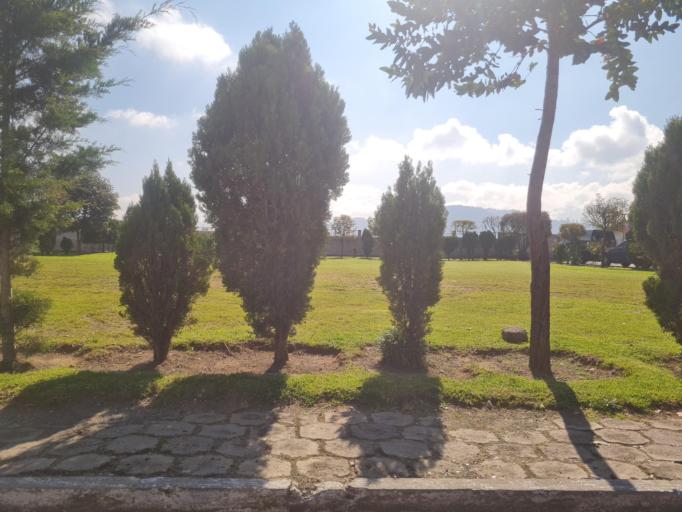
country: GT
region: Quetzaltenango
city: Quetzaltenango
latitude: 14.8403
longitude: -91.5315
